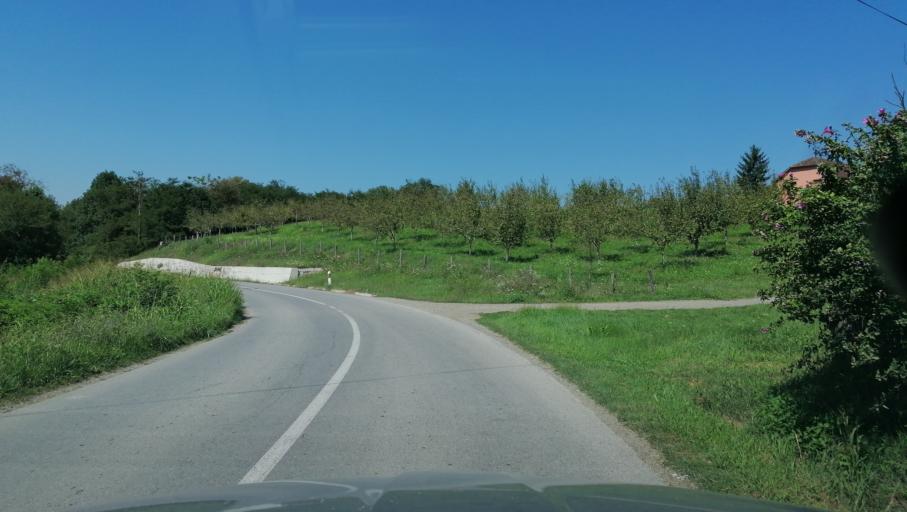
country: RS
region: Central Serbia
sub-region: Raski Okrug
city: Vrnjacka Banja
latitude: 43.7062
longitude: 20.8439
